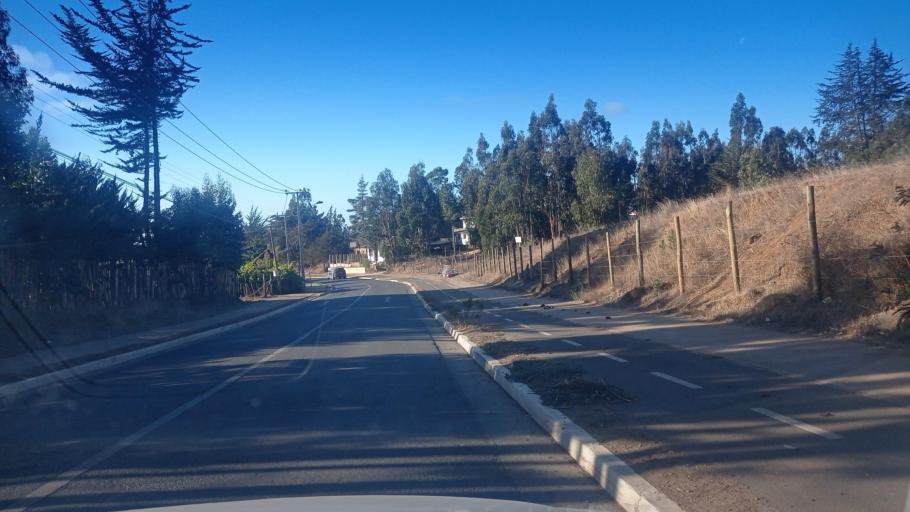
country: CL
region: O'Higgins
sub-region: Provincia de Colchagua
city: Santa Cruz
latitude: -34.4110
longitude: -71.9957
